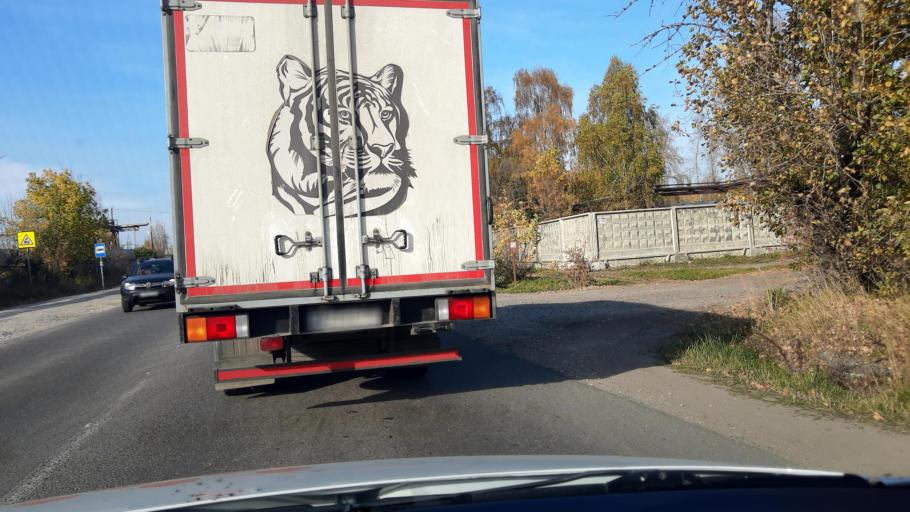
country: RU
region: Moskovskaya
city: Elektrostal'
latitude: 55.7733
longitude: 38.4707
